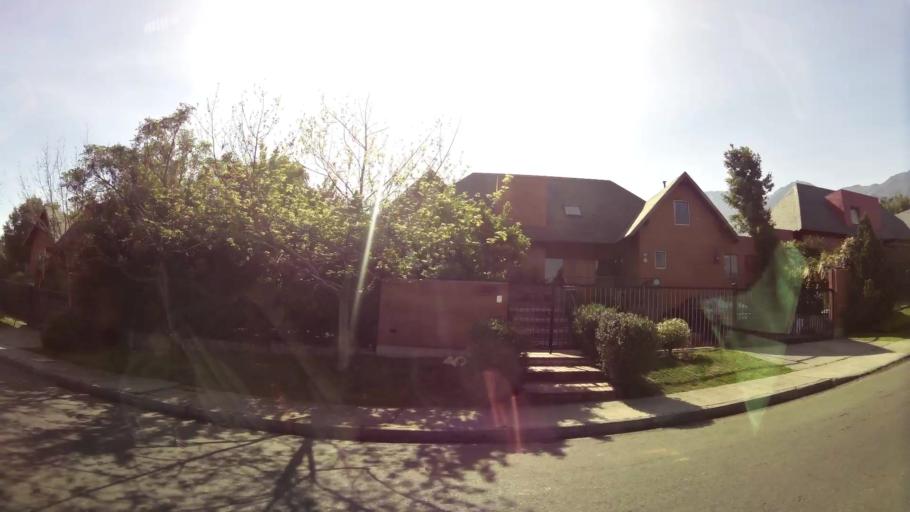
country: CL
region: Santiago Metropolitan
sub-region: Provincia de Santiago
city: Villa Presidente Frei, Nunoa, Santiago, Chile
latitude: -33.4967
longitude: -70.5267
